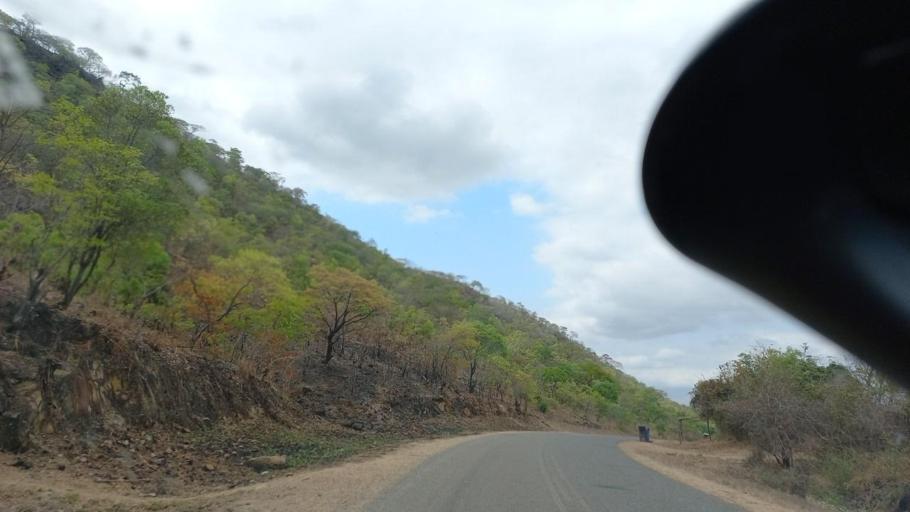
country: ZM
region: Lusaka
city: Luangwa
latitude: -15.0642
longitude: 29.7288
